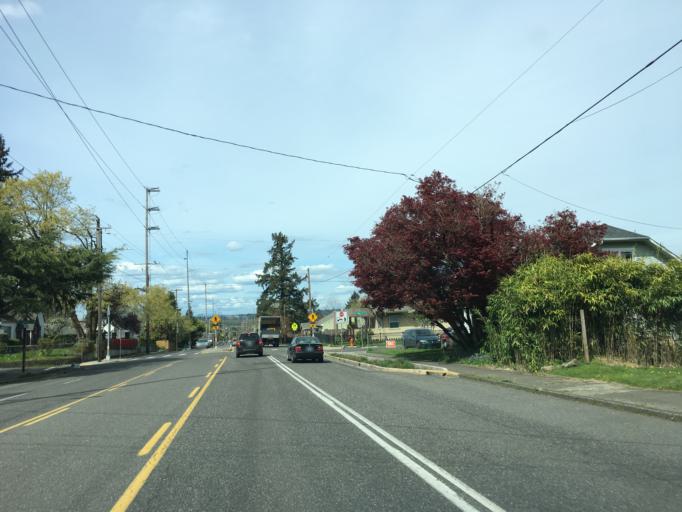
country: US
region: Oregon
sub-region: Multnomah County
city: Lents
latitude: 45.5531
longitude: -122.5578
